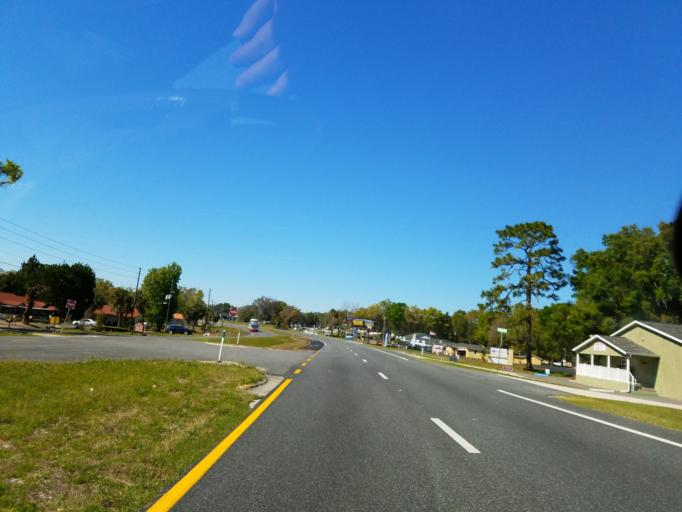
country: US
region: Florida
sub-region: Marion County
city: Belleview
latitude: 29.0539
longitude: -82.0468
